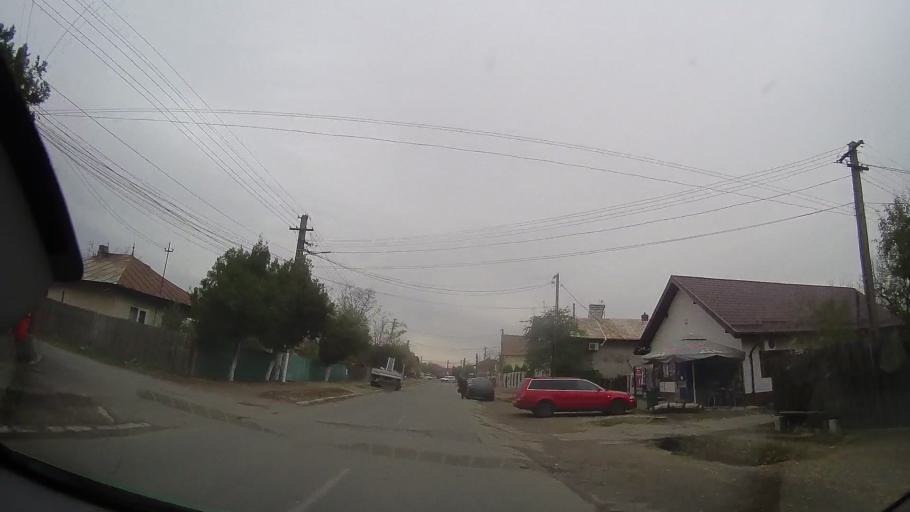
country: RO
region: Prahova
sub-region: Comuna Ceptura
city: Ceptura de Jos
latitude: 45.0145
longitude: 26.3321
